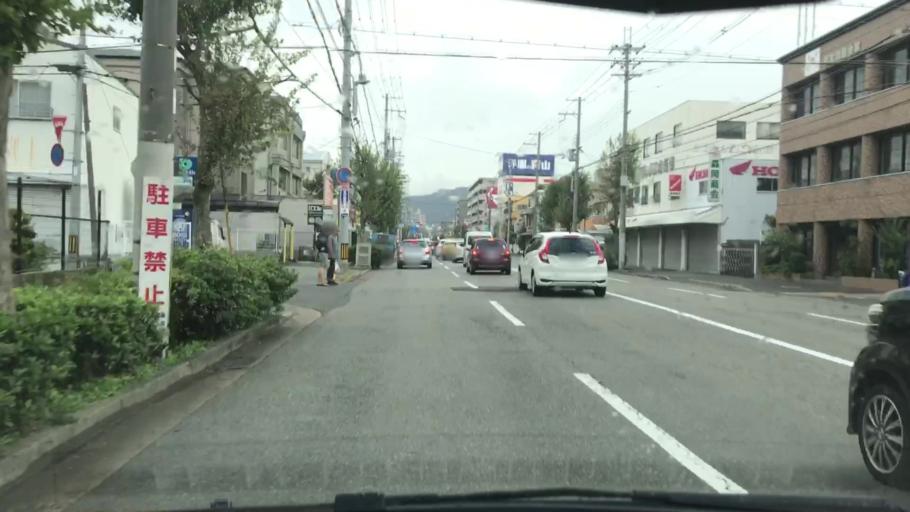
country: JP
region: Hyogo
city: Nishinomiya-hama
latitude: 34.7421
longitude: 135.3466
